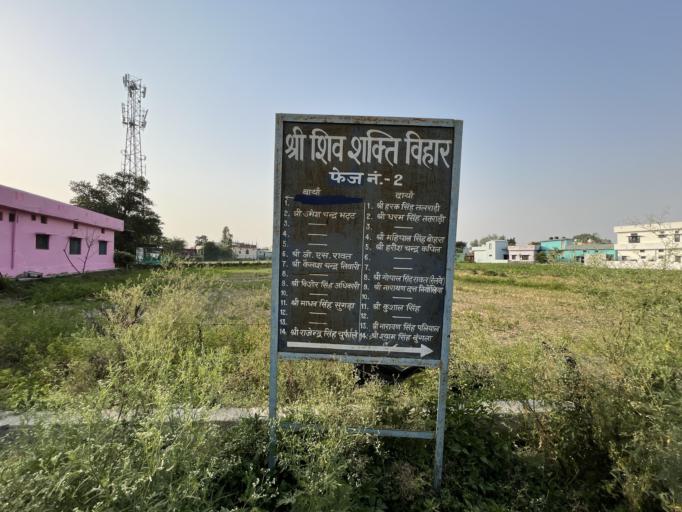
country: IN
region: Uttarakhand
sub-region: Naini Tal
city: Haldwani
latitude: 29.2325
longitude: 79.5174
